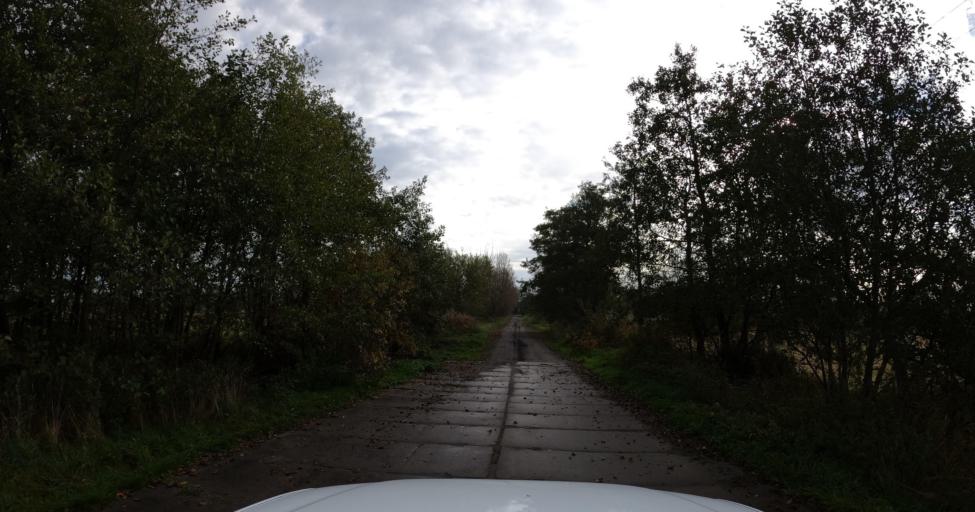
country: PL
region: West Pomeranian Voivodeship
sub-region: Powiat kamienski
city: Kamien Pomorski
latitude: 53.9860
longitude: 14.8498
